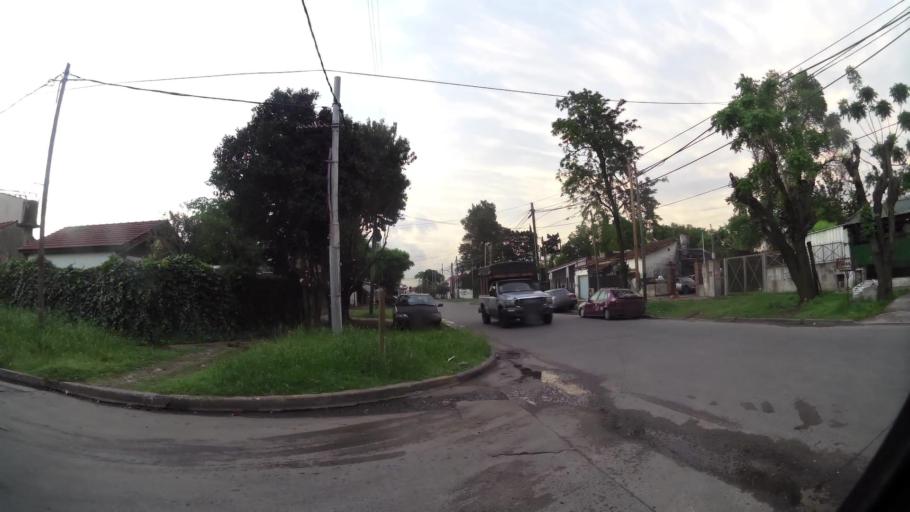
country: AR
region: Buenos Aires
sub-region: Partido de Lomas de Zamora
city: Lomas de Zamora
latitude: -34.7545
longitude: -58.3688
